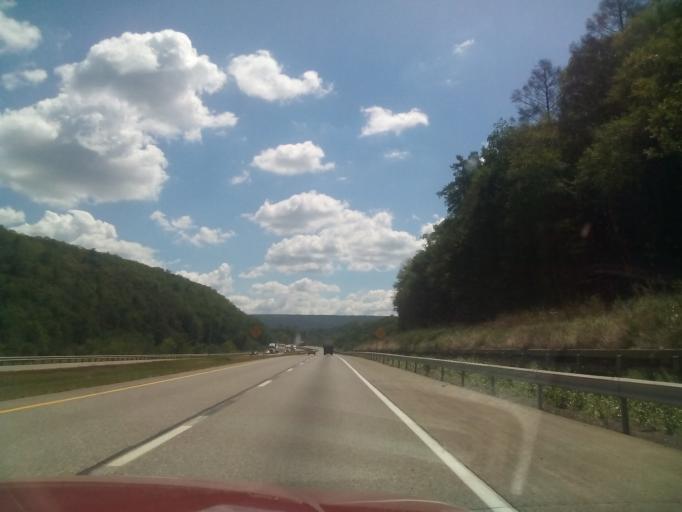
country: US
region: Pennsylvania
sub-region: Luzerne County
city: Nescopeck
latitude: 41.0112
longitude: -76.1669
